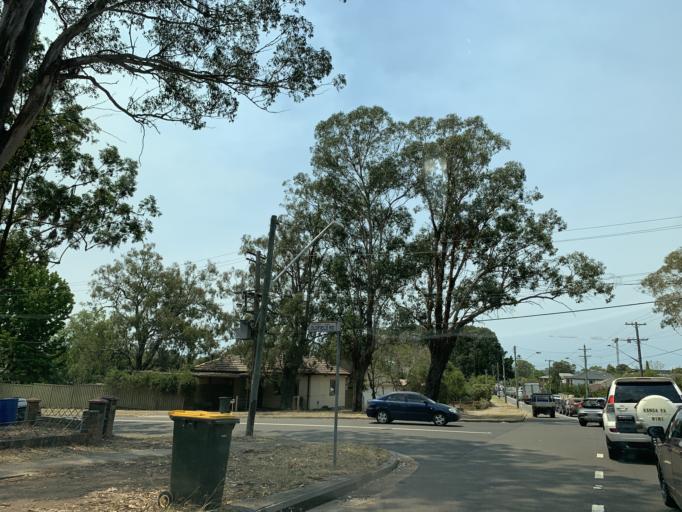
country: AU
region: New South Wales
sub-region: Blacktown
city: Blacktown
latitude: -33.7799
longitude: 150.9298
